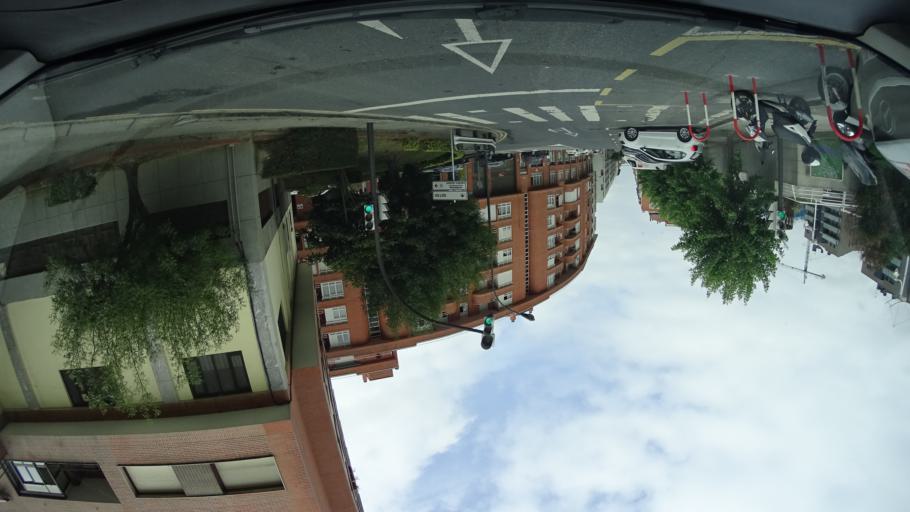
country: ES
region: Basque Country
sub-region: Bizkaia
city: Bilbao
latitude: 43.2738
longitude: -2.9607
